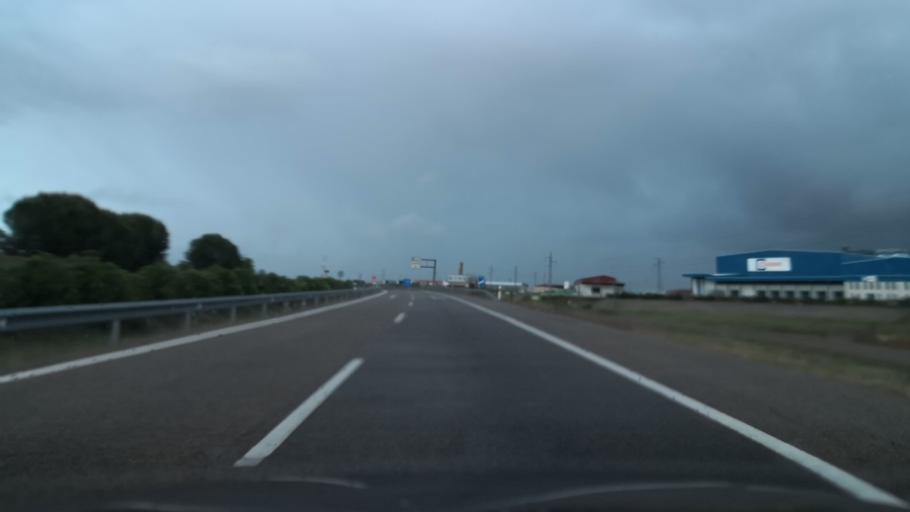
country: ES
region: Extremadura
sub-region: Provincia de Badajoz
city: Lobon
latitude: 38.8395
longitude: -6.6264
